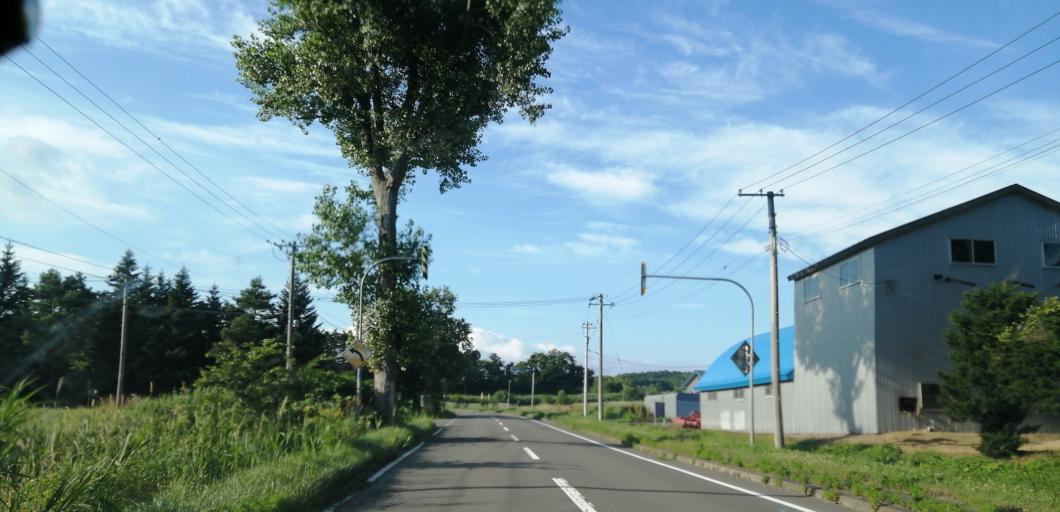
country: JP
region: Hokkaido
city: Chitose
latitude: 42.9136
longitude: 141.7274
